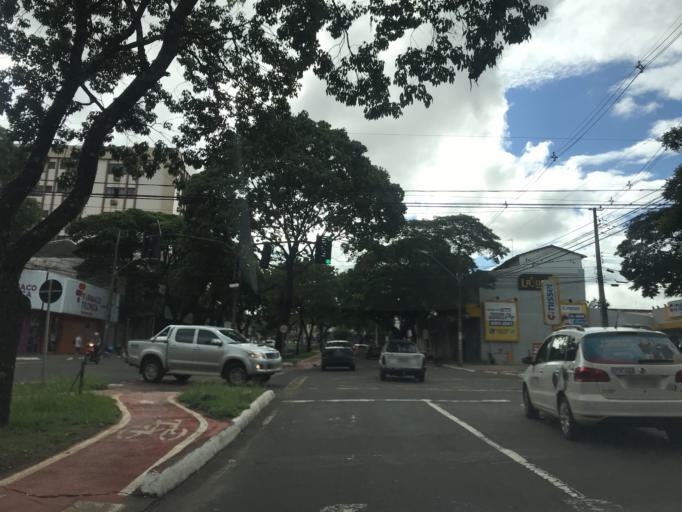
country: BR
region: Parana
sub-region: Maringa
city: Maringa
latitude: -23.4207
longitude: -51.9448
